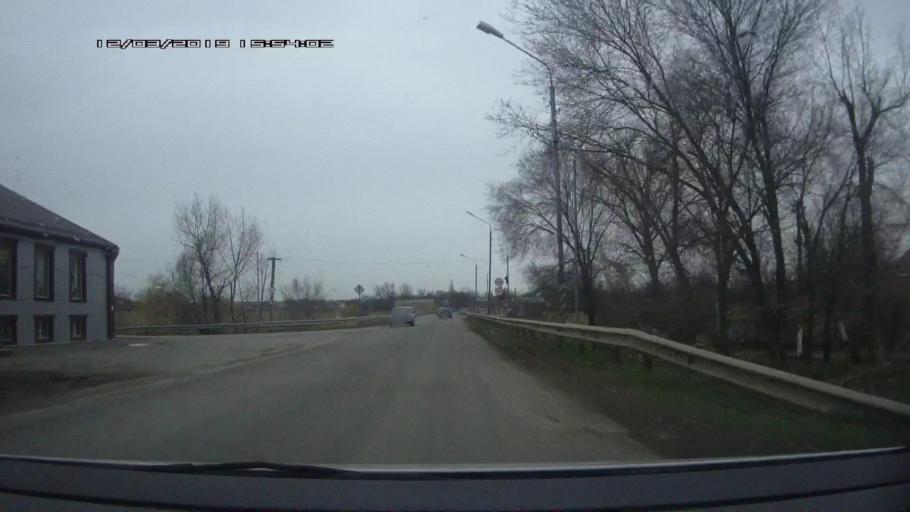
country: RU
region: Rostov
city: Novobataysk
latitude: 46.8883
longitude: 39.7769
